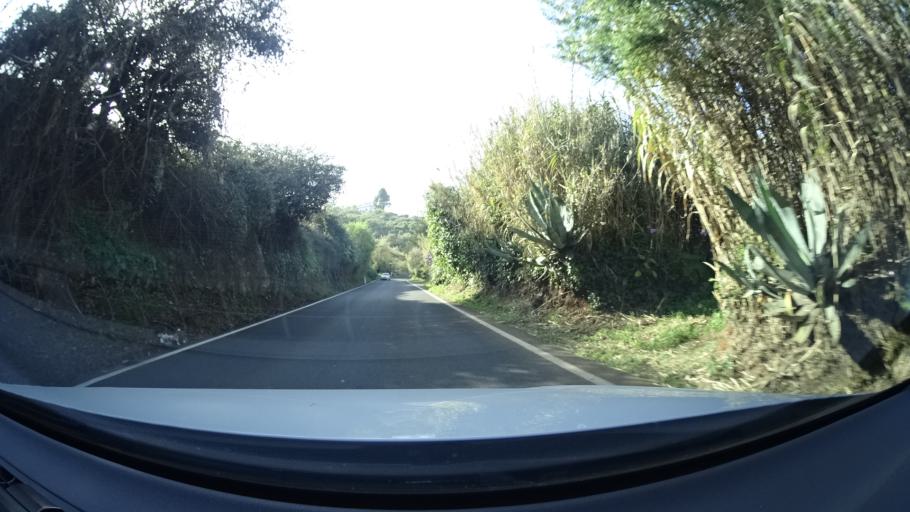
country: ES
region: Canary Islands
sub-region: Provincia de Las Palmas
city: Vega de San Mateo
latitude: 28.0162
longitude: -15.5388
